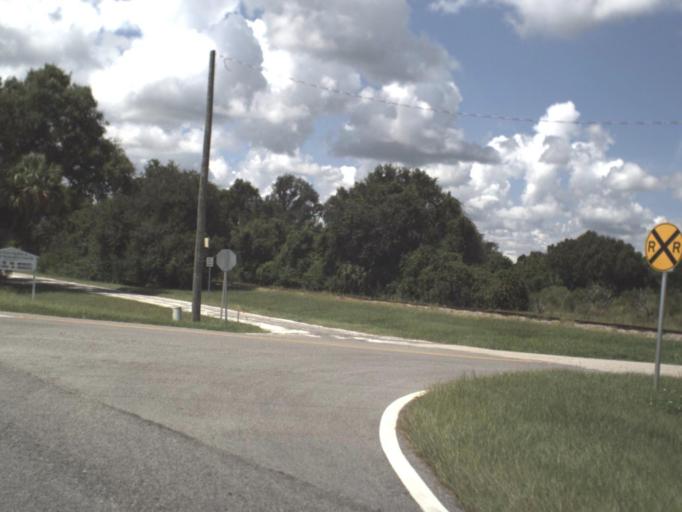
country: US
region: Florida
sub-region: DeSoto County
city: Nocatee
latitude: 27.0850
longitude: -81.9550
